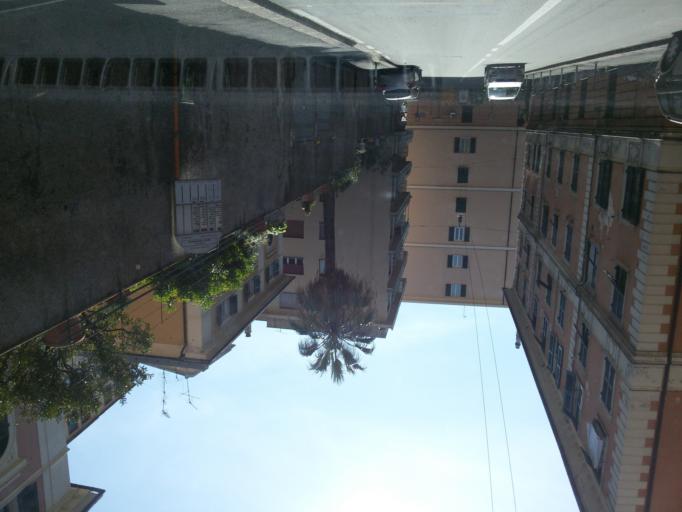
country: IT
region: Liguria
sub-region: Provincia di Genova
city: Genoa
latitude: 44.4195
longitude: 8.9229
